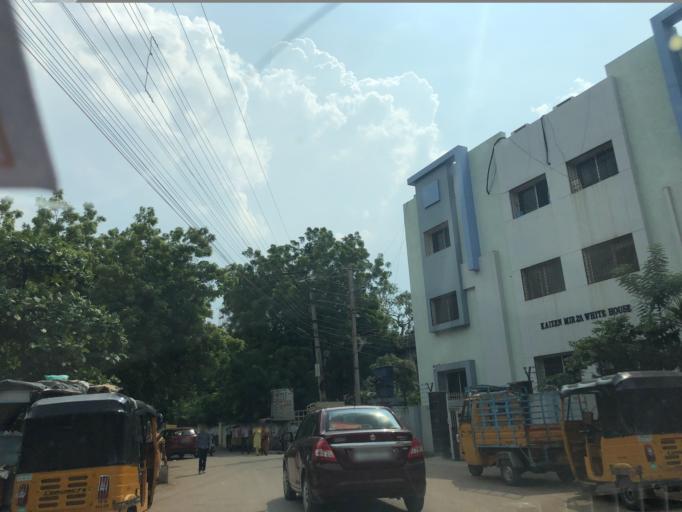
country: IN
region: Telangana
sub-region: Hyderabad
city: Malkajgiri
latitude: 17.4448
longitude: 78.4777
